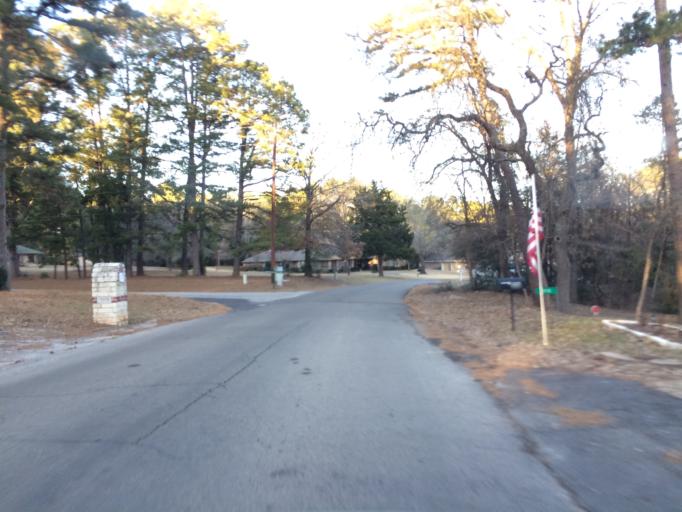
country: US
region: Texas
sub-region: Wood County
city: Hawkins
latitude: 32.7265
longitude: -95.1912
